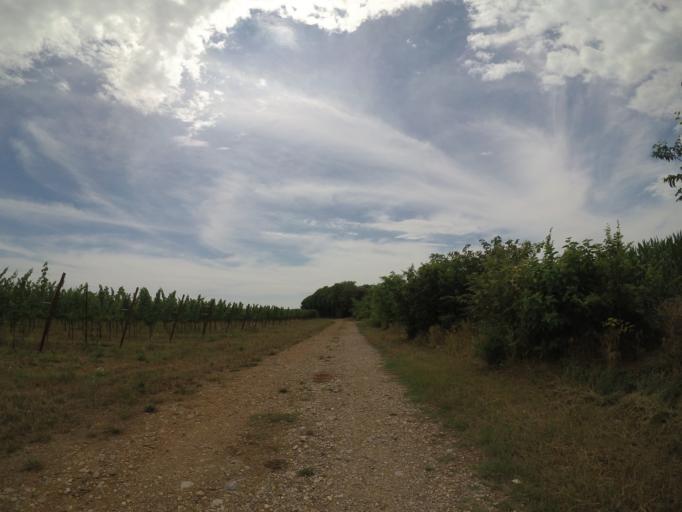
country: IT
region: Friuli Venezia Giulia
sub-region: Provincia di Udine
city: Bertiolo
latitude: 45.9615
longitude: 13.0584
